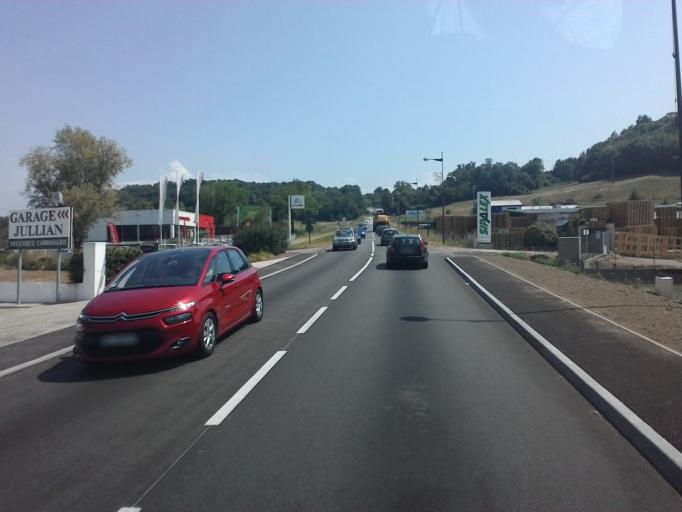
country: FR
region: Rhone-Alpes
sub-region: Departement de l'Isere
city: Les Abrets
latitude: 45.5266
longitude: 5.5924
